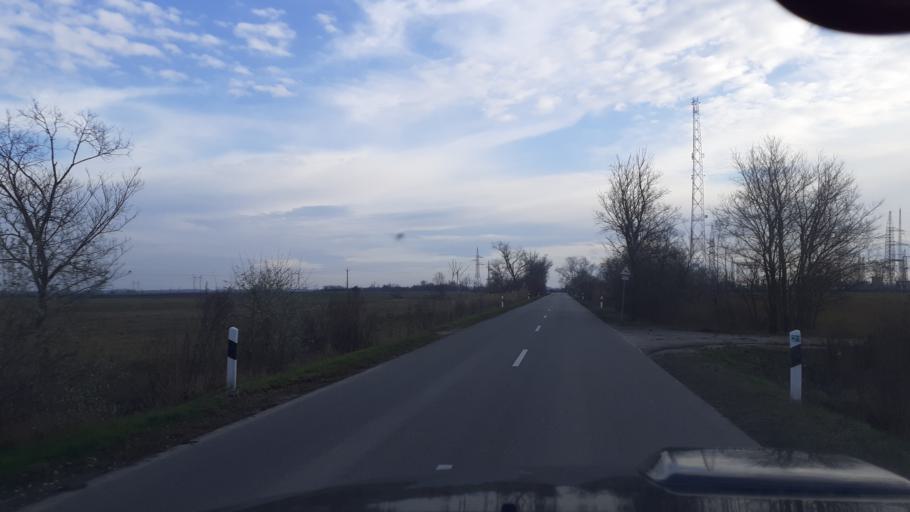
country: HU
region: Bacs-Kiskun
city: Szabadszallas
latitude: 46.9259
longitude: 19.1764
